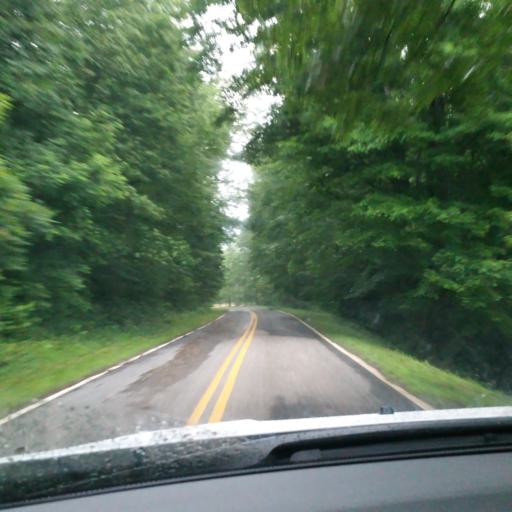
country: US
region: North Carolina
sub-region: Yancey County
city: Burnsville
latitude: 35.8293
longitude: -82.2072
